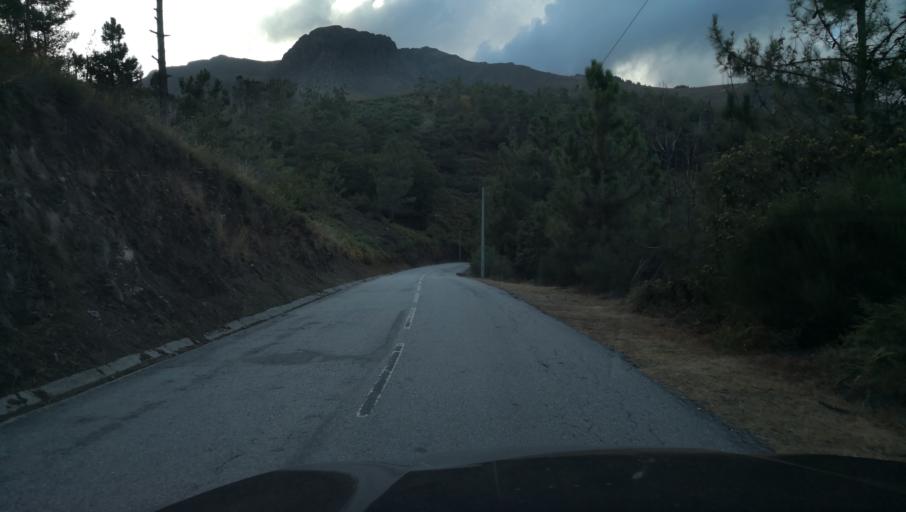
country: PT
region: Vila Real
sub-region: Santa Marta de Penaguiao
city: Santa Marta de Penaguiao
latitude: 41.2371
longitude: -7.8483
